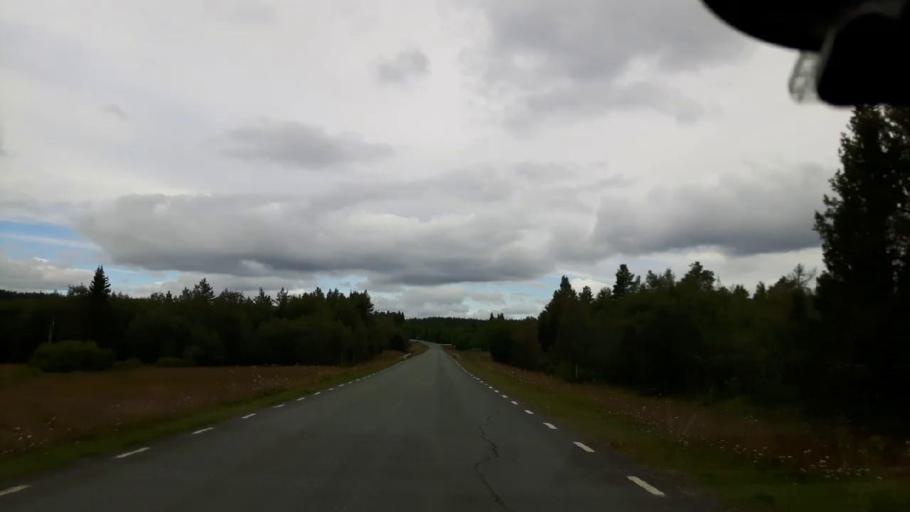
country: SE
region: Jaemtland
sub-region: Krokoms Kommun
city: Valla
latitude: 63.5655
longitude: 13.8437
